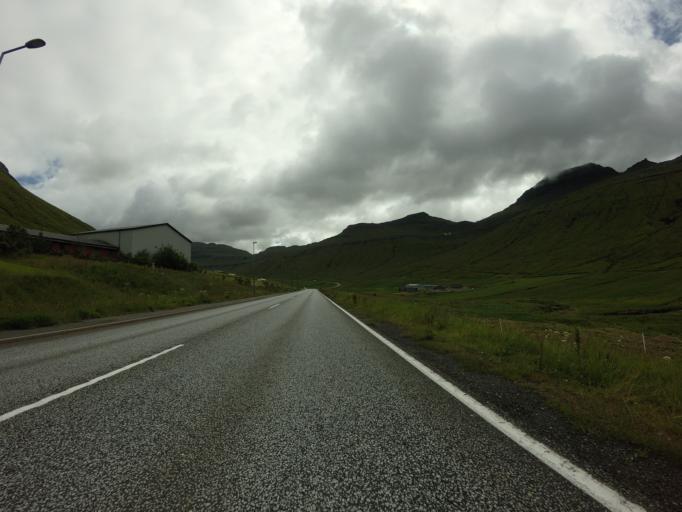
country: FO
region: Streymoy
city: Kollafjordhur
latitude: 62.1089
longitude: -6.9660
